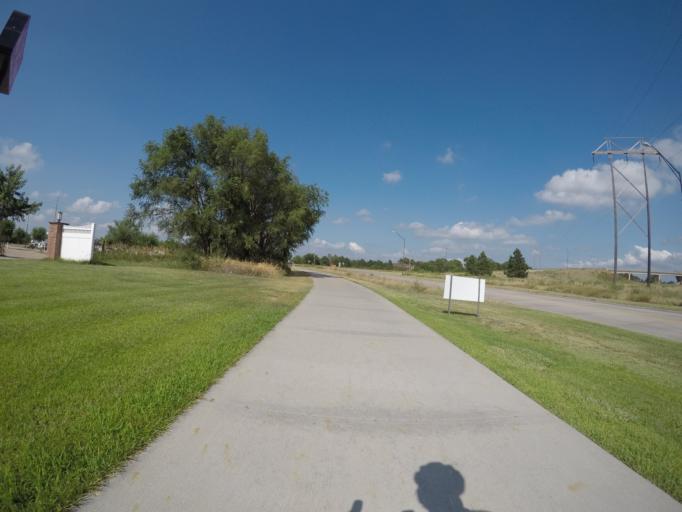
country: US
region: Nebraska
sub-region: Buffalo County
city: Kearney
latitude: 40.6706
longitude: -99.0686
